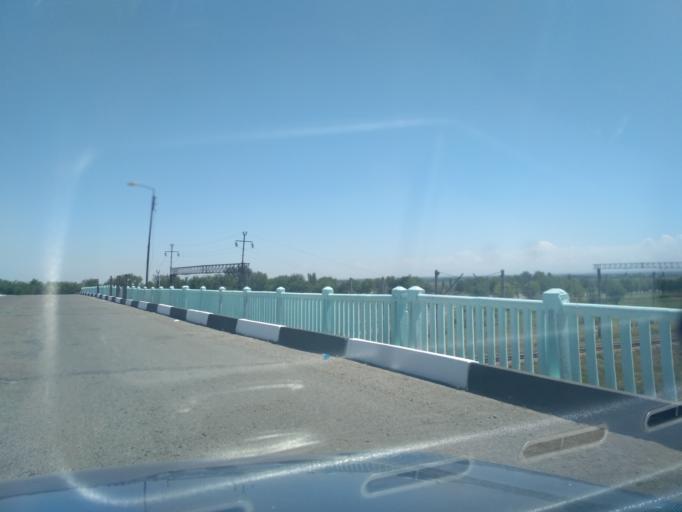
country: UZ
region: Sirdaryo
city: Yangiyer
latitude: 40.2383
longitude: 68.8421
